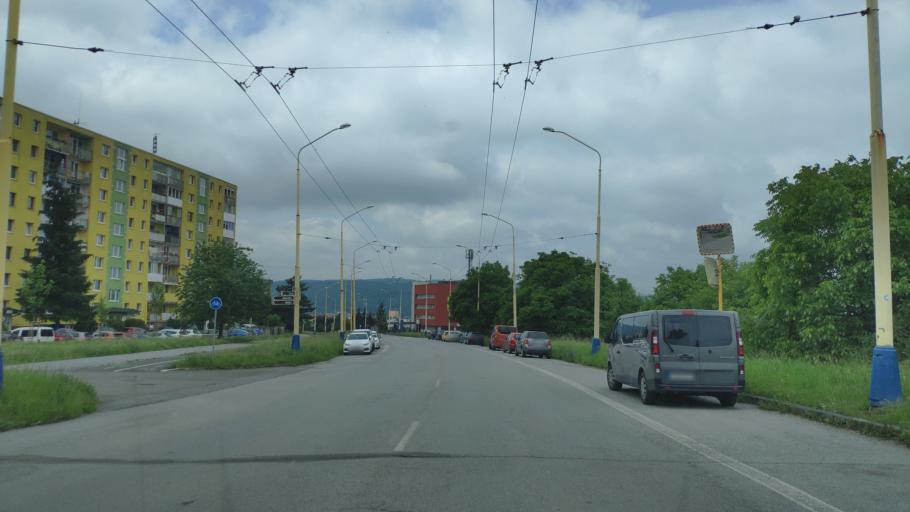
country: SK
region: Presovsky
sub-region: Okres Presov
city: Presov
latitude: 48.9932
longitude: 21.2737
